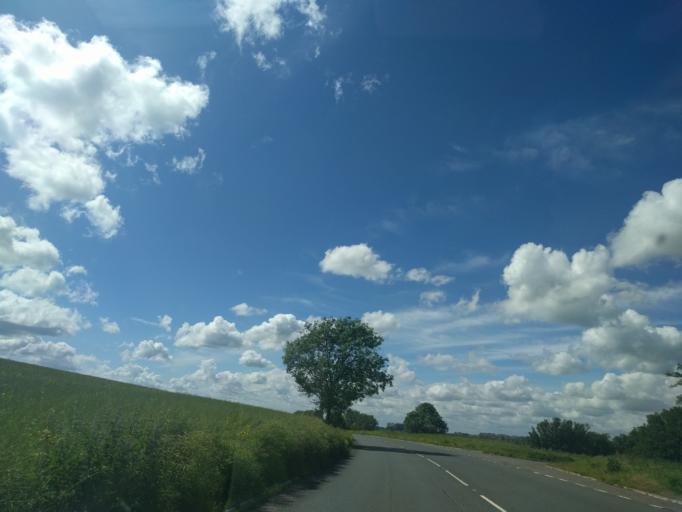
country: GB
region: England
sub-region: Wiltshire
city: Avebury
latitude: 51.4270
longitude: -1.8996
